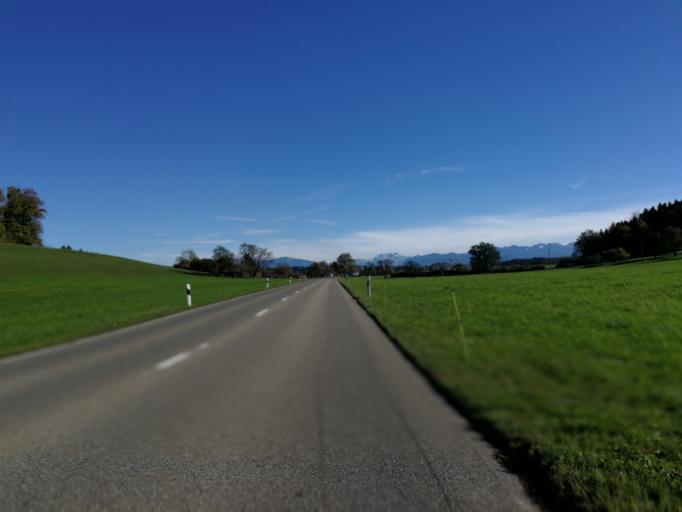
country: CH
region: Zurich
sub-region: Bezirk Hinwil
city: Binzikon
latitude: 47.2865
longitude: 8.7473
